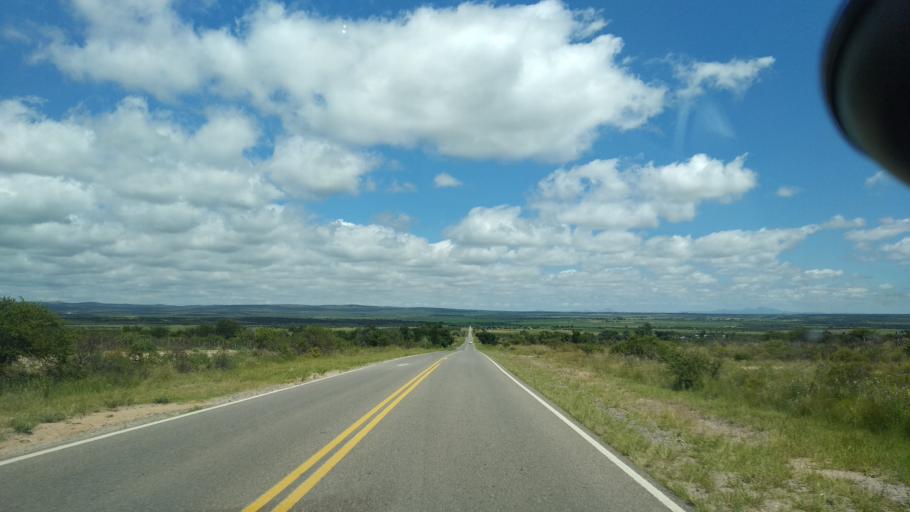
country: AR
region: Cordoba
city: Villa Cura Brochero
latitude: -31.6898
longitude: -65.0726
